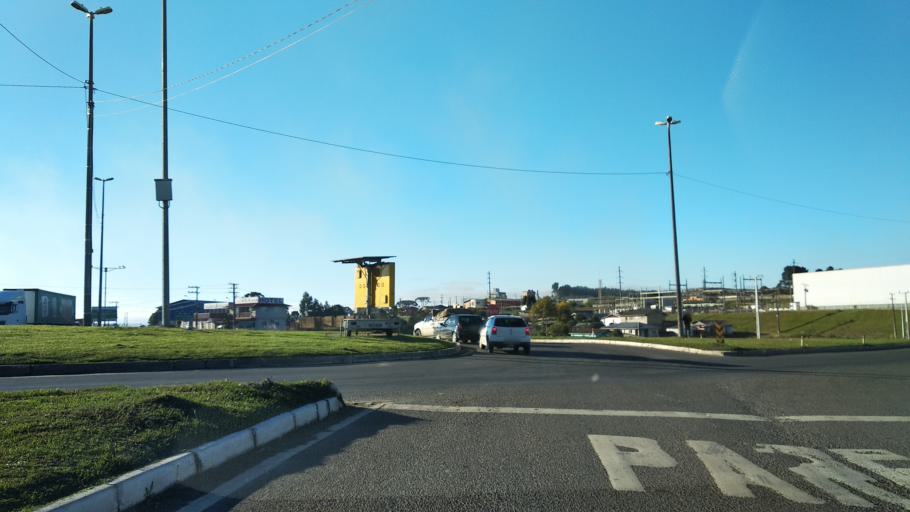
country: BR
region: Santa Catarina
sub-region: Lages
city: Lages
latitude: -27.7999
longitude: -50.3638
